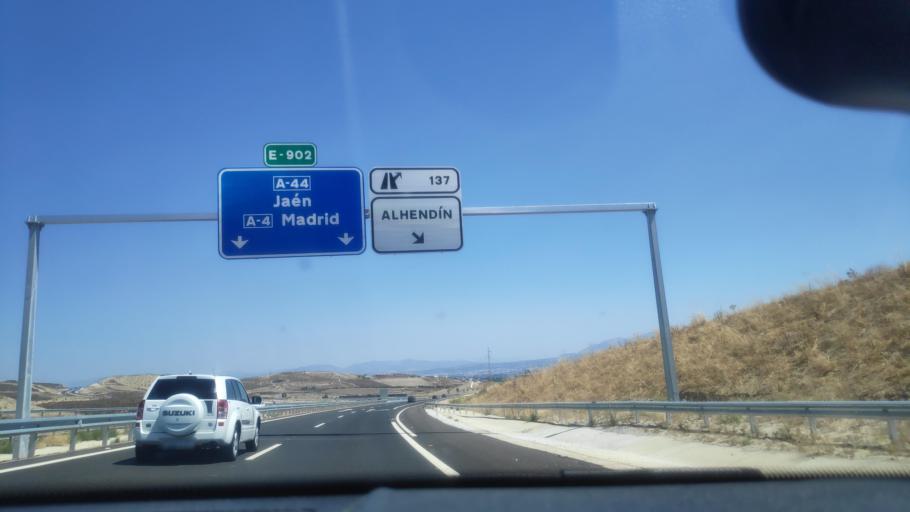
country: ES
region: Andalusia
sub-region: Provincia de Granada
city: Alhendin
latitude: 37.0972
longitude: -3.6738
